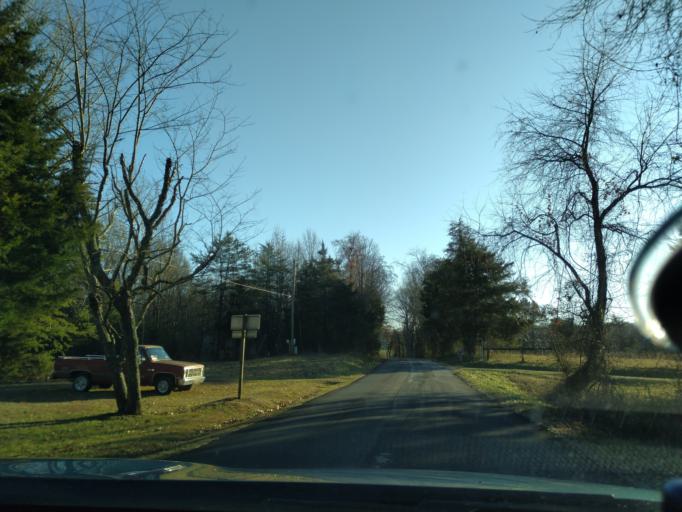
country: US
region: Virginia
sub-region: Prince Edward County
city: Hampden Sydney
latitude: 37.3343
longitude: -78.5789
